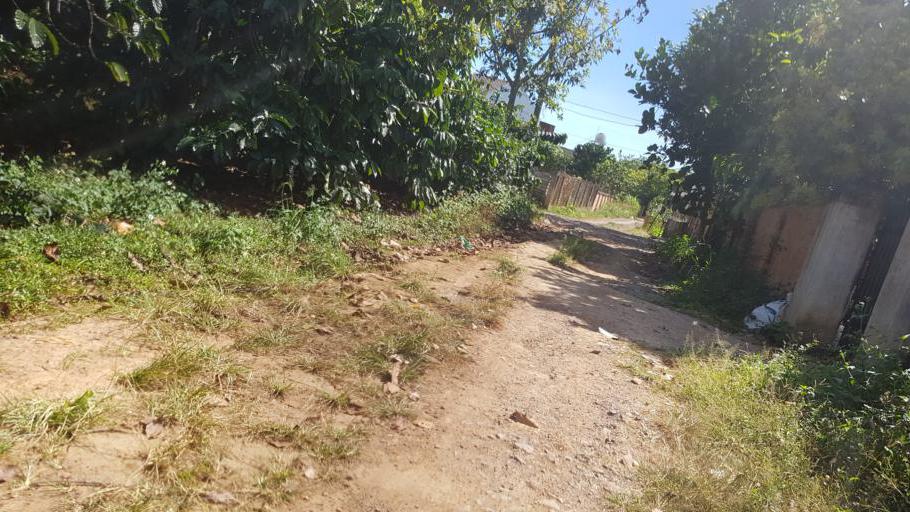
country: VN
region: Lam Dong
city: Da Lat
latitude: 11.8819
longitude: 108.3414
